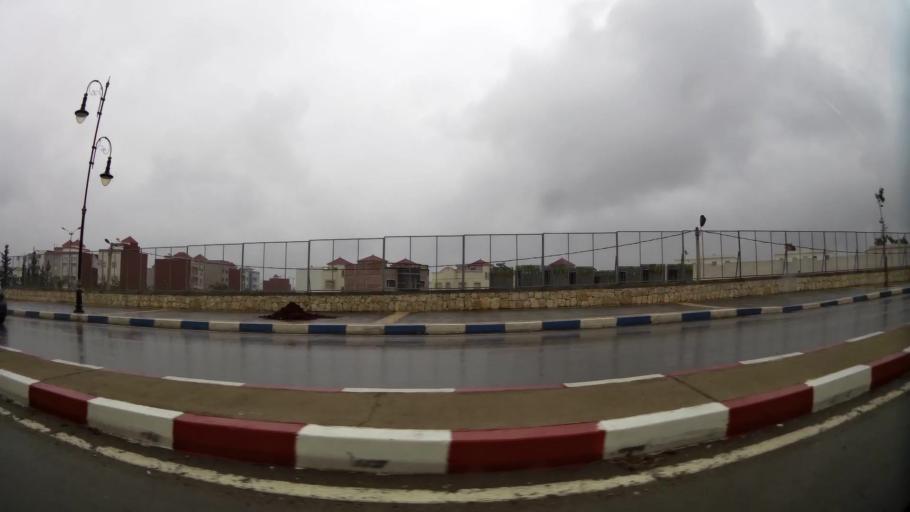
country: MA
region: Taza-Al Hoceima-Taounate
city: Imzourene
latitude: 35.1494
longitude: -3.8450
